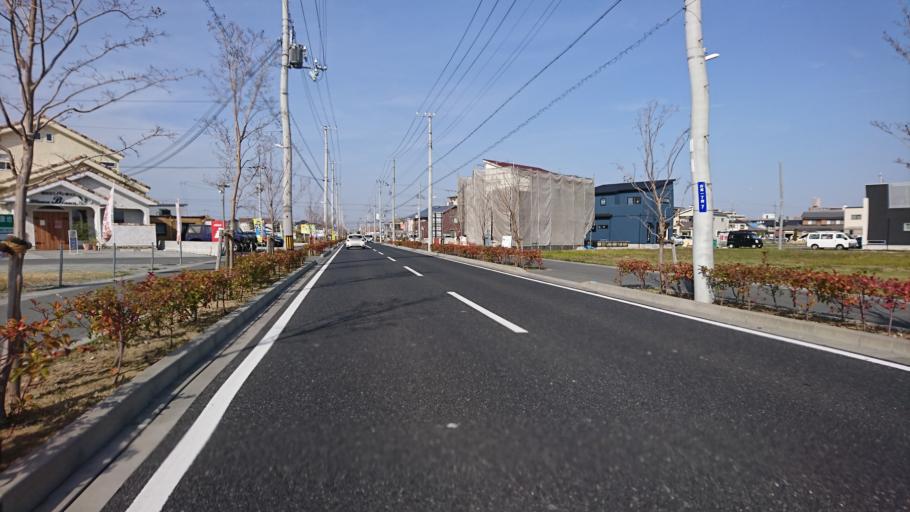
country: JP
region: Hyogo
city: Kakogawacho-honmachi
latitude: 34.7112
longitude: 134.8697
